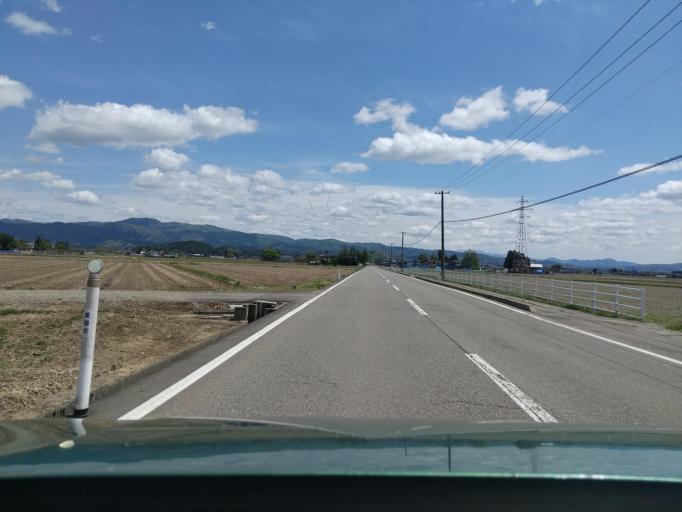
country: JP
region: Akita
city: Omagari
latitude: 39.3861
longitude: 140.5121
